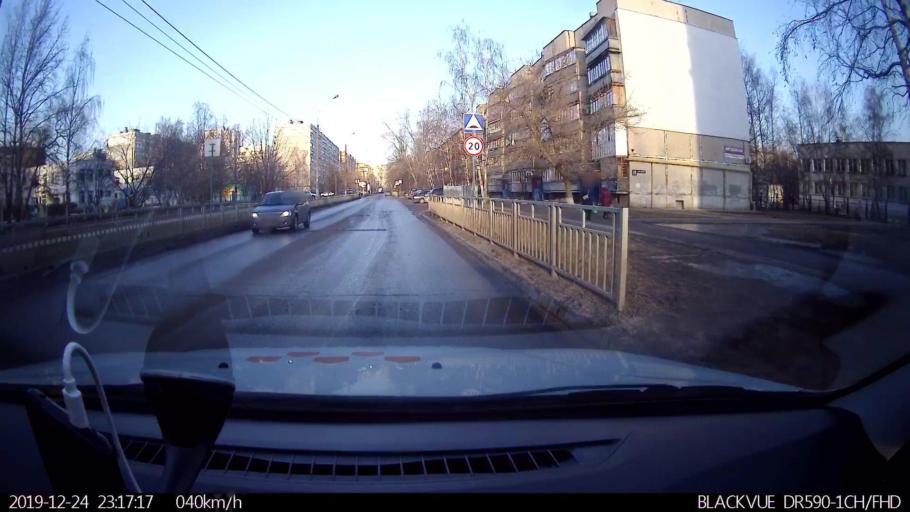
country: RU
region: Nizjnij Novgorod
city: Gorbatovka
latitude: 56.2543
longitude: 43.8588
